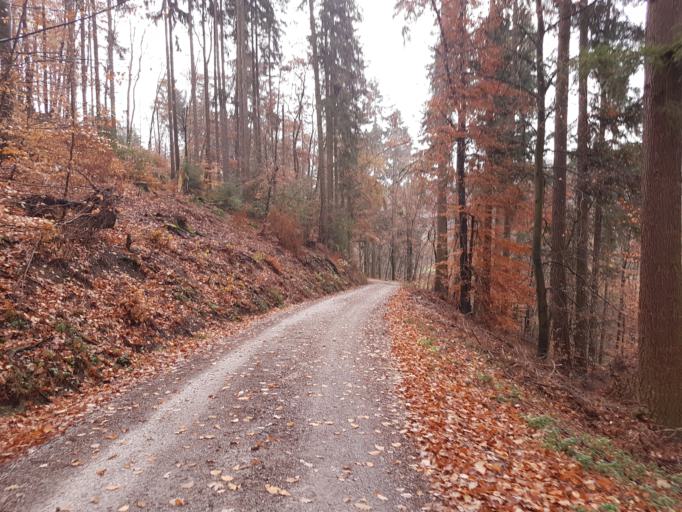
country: DE
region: Hesse
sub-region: Regierungsbezirk Darmstadt
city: Kiedrich
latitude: 50.0542
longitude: 8.0400
